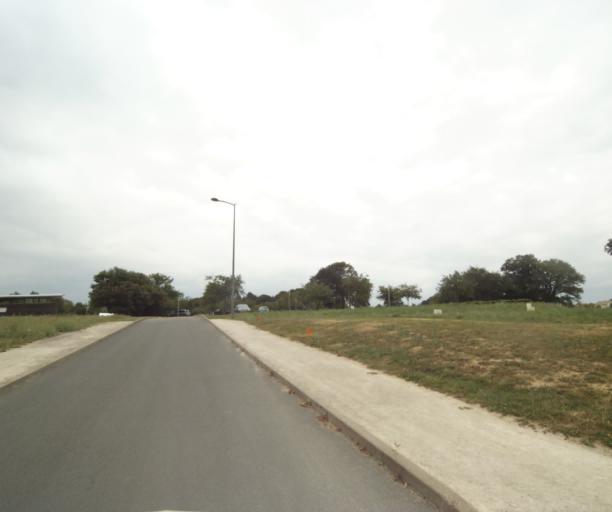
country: FR
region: Pays de la Loire
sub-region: Departement de la Sarthe
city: Sable-sur-Sarthe
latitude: 47.8267
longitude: -0.3270
